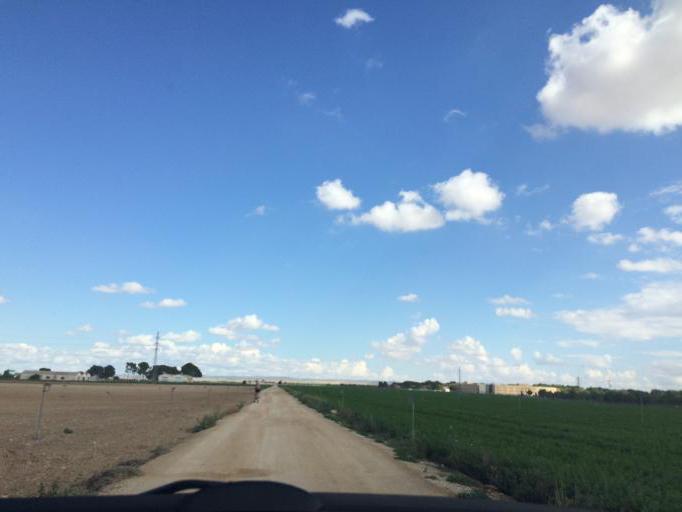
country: ES
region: Castille-La Mancha
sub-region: Provincia de Albacete
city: Albacete
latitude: 38.9586
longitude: -1.8731
